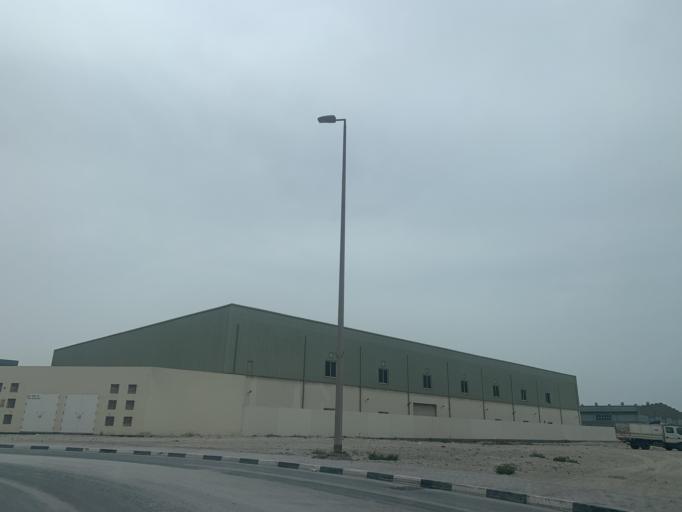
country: BH
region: Muharraq
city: Al Hadd
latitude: 26.2150
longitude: 50.6795
